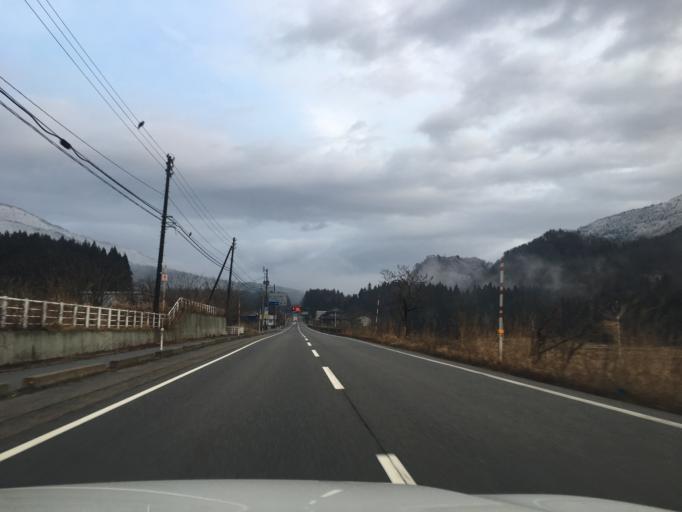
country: JP
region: Niigata
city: Murakami
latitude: 38.3589
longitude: 139.5524
